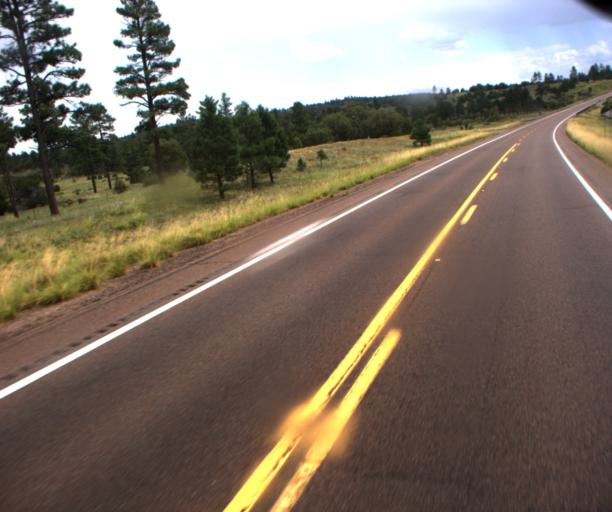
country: US
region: Arizona
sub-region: Navajo County
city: Linden
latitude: 34.3644
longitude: -110.3362
